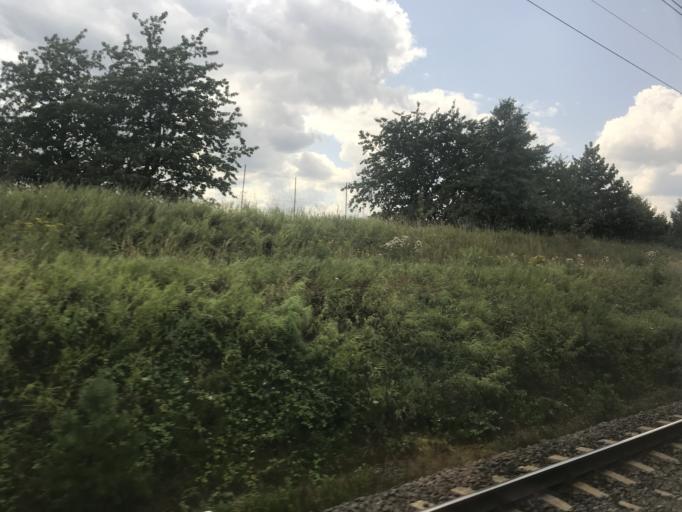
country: PL
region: Lubusz
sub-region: Powiat sulecinski
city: Torzym
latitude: 52.3194
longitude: 15.0230
